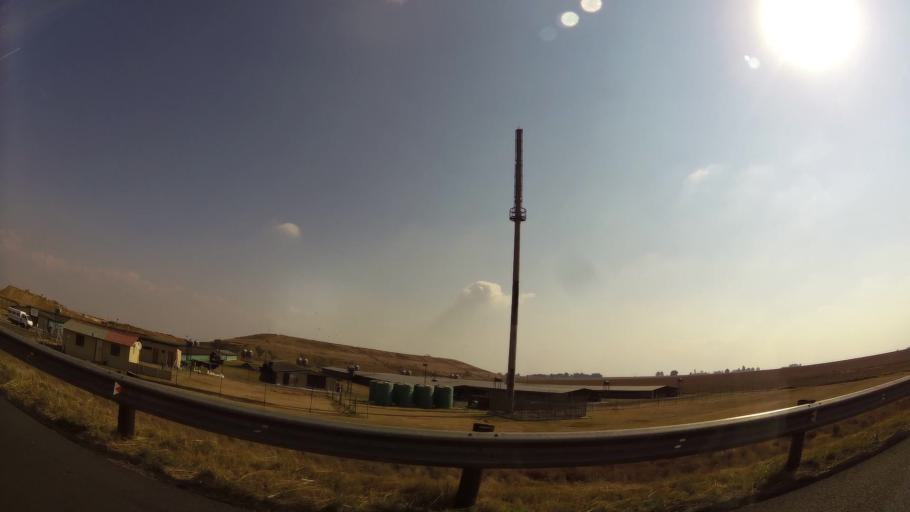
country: ZA
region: Mpumalanga
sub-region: Nkangala District Municipality
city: Delmas
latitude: -26.1516
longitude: 28.5272
